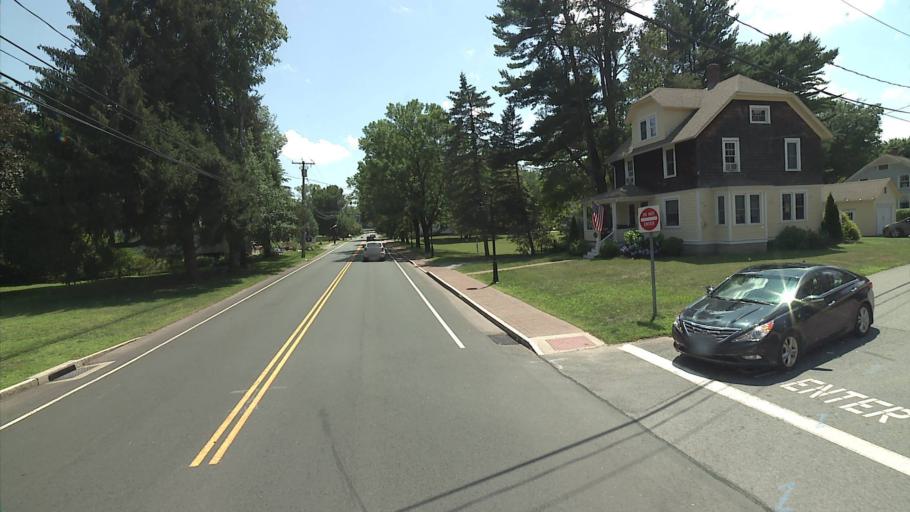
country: US
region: Connecticut
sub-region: Middlesex County
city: Deep River Center
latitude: 41.3835
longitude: -72.4351
